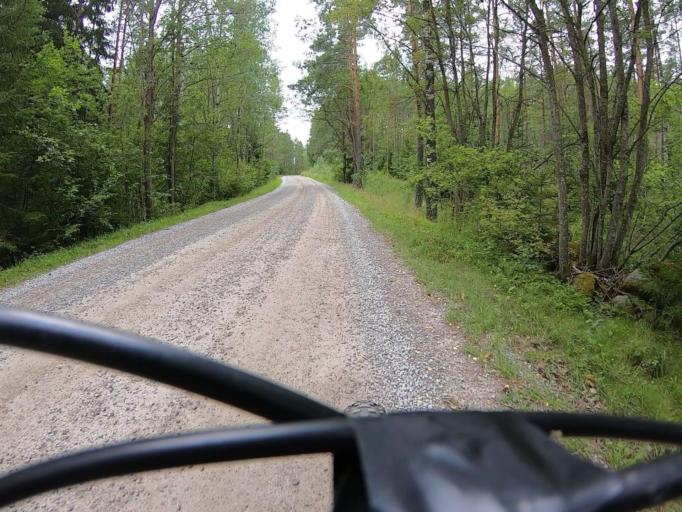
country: FI
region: Varsinais-Suomi
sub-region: Vakka-Suomi
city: Uusikaupunki
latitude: 60.8454
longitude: 21.3904
